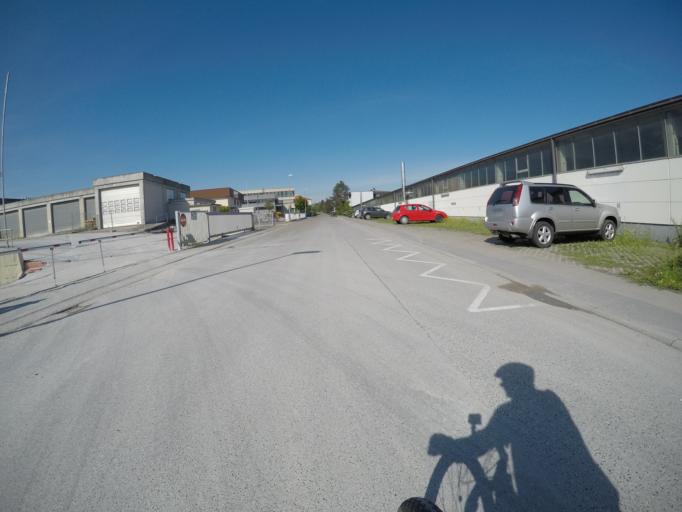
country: DE
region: Baden-Wuerttemberg
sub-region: Regierungsbezirk Stuttgart
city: Gartringen
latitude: 48.6381
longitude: 8.9129
